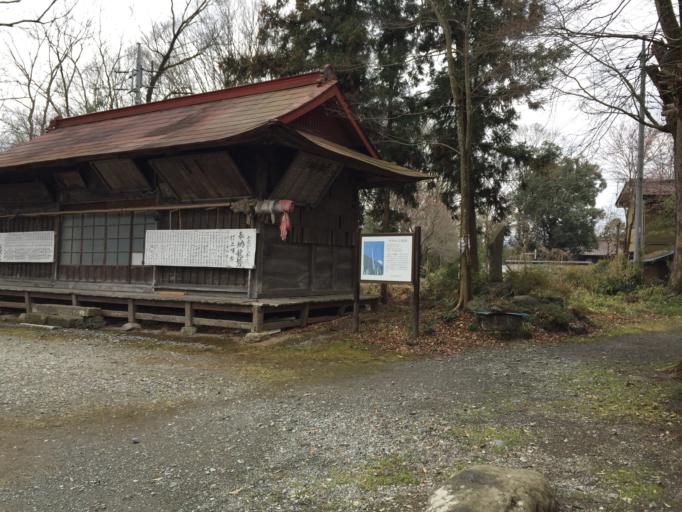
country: JP
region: Saitama
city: Chichibu
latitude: 36.0451
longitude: 139.0333
